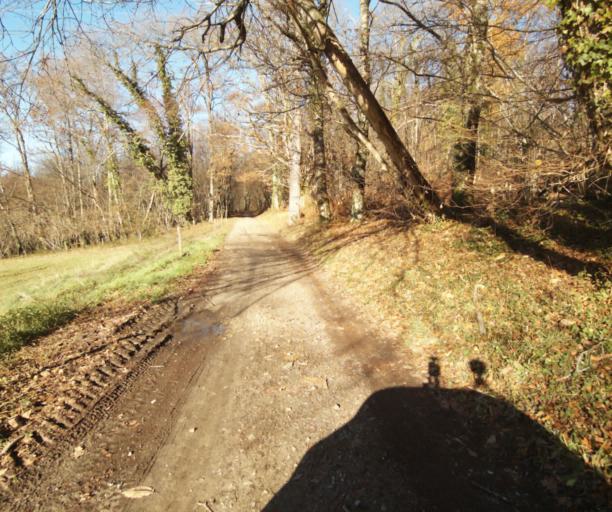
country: FR
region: Limousin
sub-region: Departement de la Correze
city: Sainte-Fortunade
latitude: 45.2160
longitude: 1.7785
